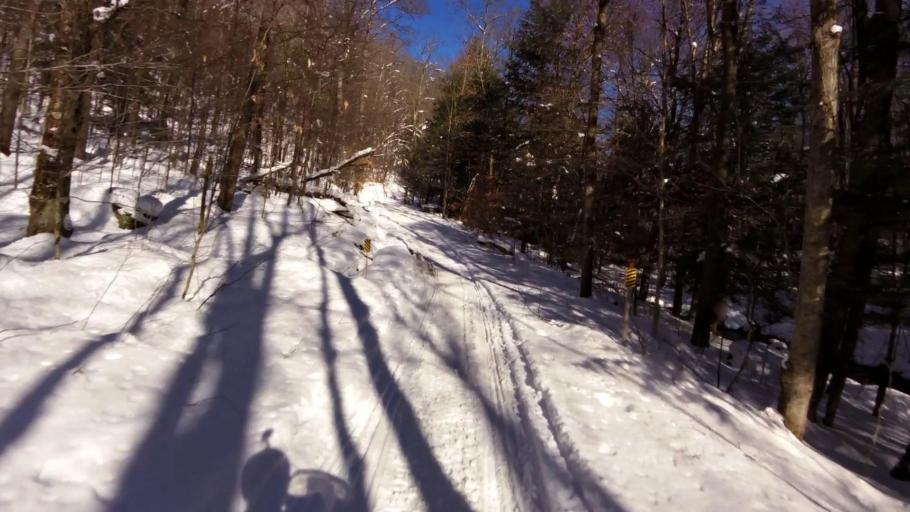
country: US
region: Pennsylvania
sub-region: McKean County
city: Bradford
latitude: 42.0114
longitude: -78.7954
